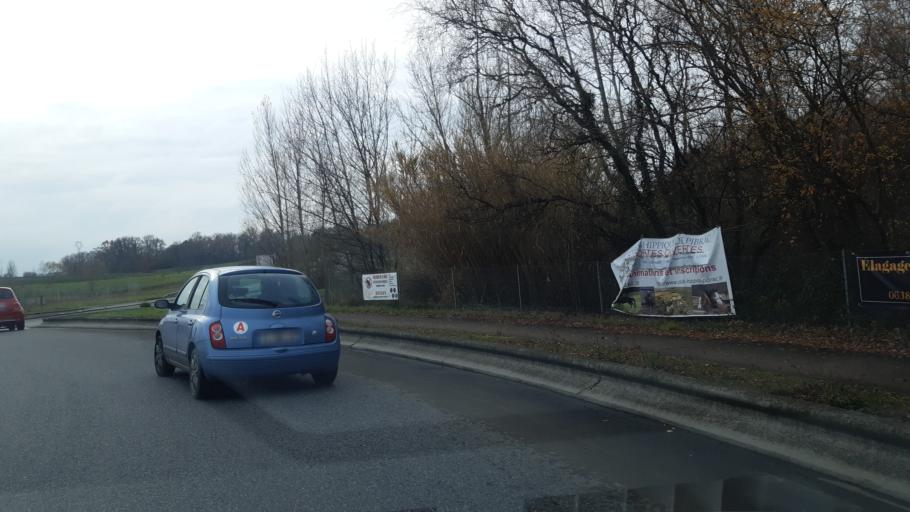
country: FR
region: Midi-Pyrenees
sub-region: Departement de la Haute-Garonne
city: Pibrac
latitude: 43.6050
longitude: 1.2821
